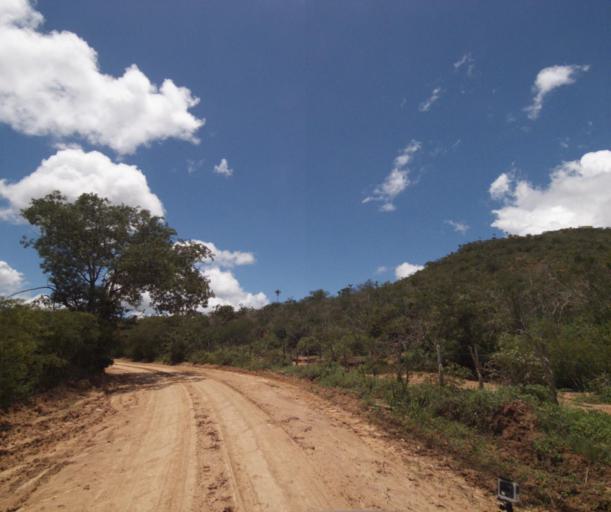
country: BR
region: Bahia
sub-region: Pocoes
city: Pocoes
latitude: -14.3808
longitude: -40.4129
